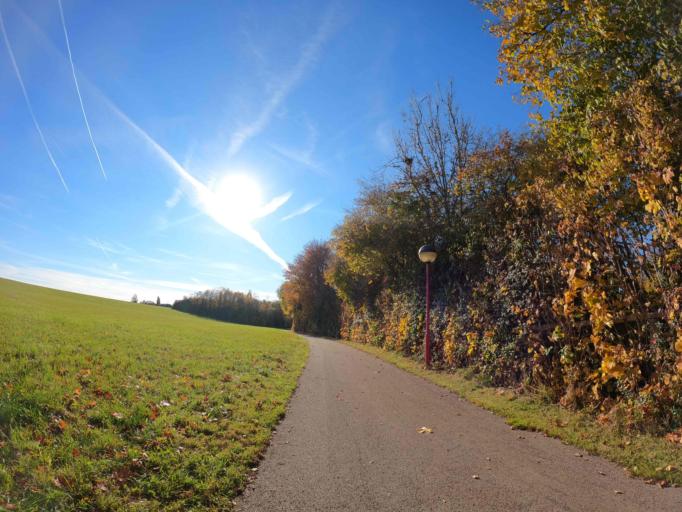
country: DE
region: Bavaria
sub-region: Upper Bavaria
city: Oberhaching
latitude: 48.0265
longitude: 11.6017
